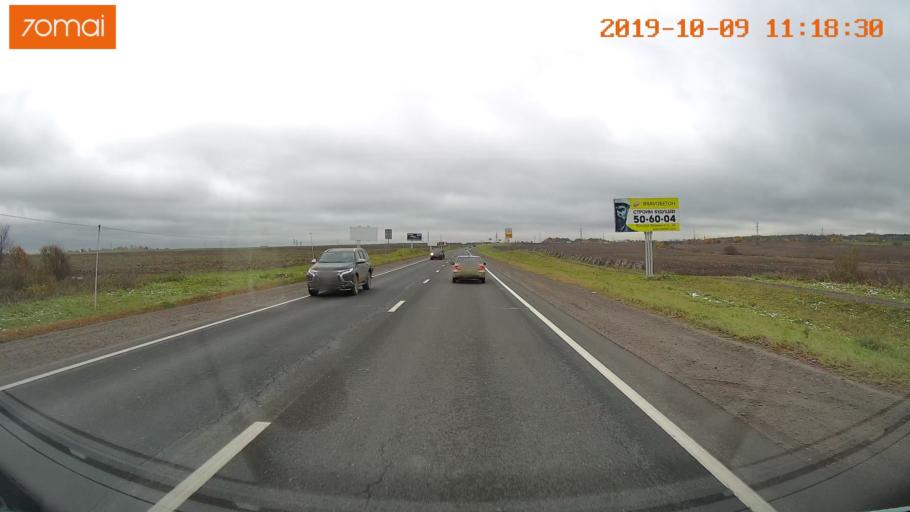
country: RU
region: Vologda
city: Vologda
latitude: 59.1675
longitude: 39.9173
